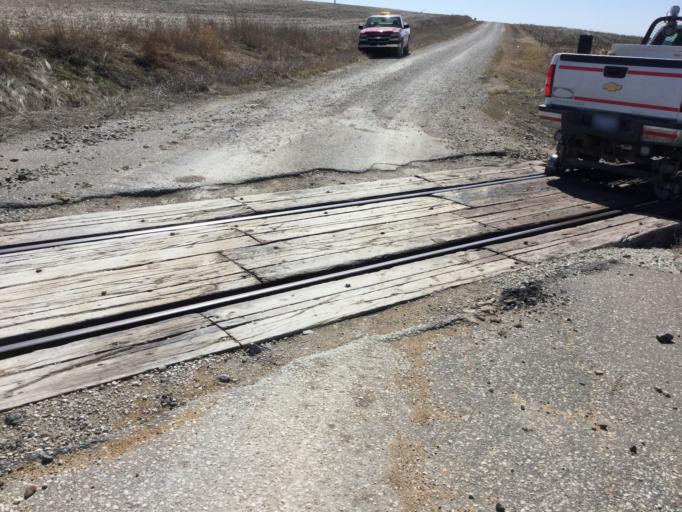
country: US
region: Kansas
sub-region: Marshall County
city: Marysville
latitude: 39.8841
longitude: -96.3891
